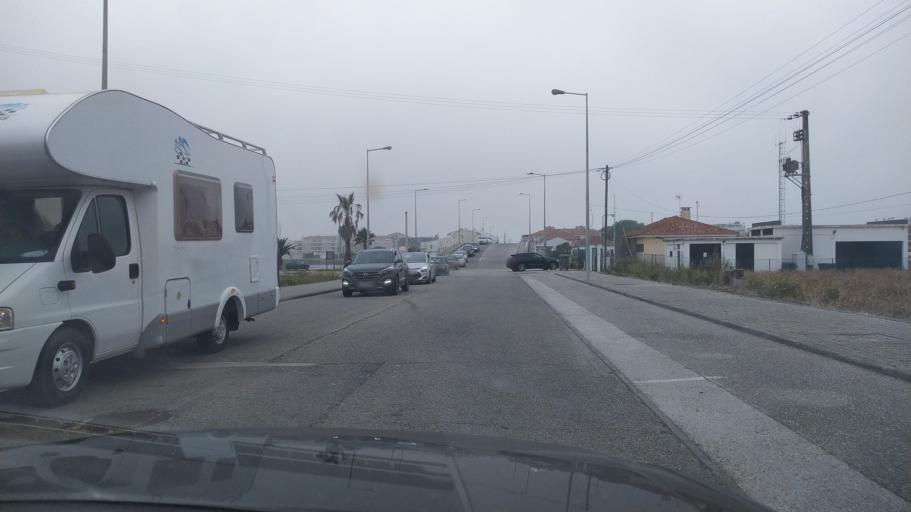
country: PT
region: Aveiro
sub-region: Ilhavo
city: Gafanha da Encarnacao
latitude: 40.5601
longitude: -8.7561
